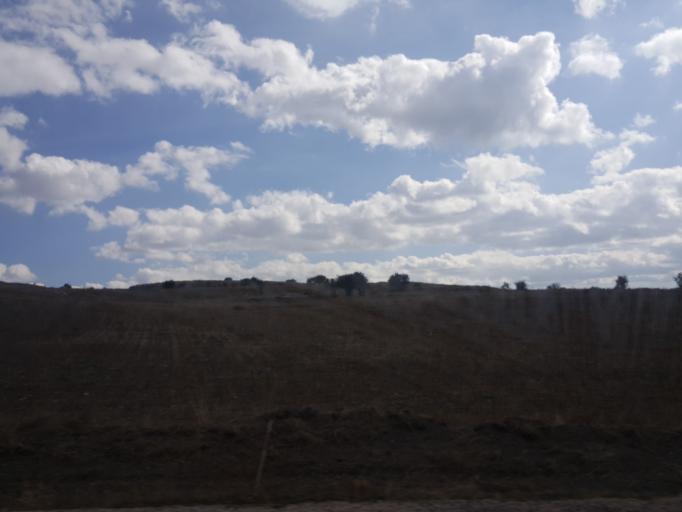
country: TR
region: Tokat
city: Artova
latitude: 40.1251
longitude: 36.3312
